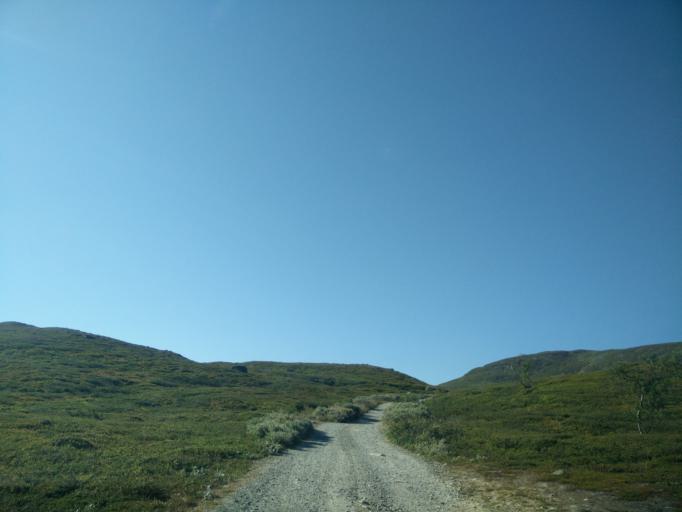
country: NO
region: Sor-Trondelag
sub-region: Tydal
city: Aas
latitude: 62.5730
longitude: 12.1997
